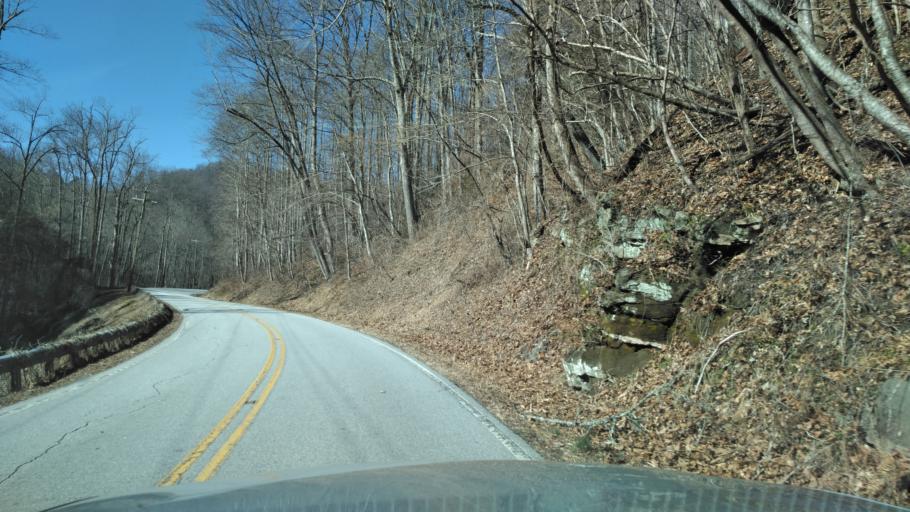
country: US
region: North Carolina
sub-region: Henderson County
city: Edneyville
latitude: 35.4586
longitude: -82.3022
